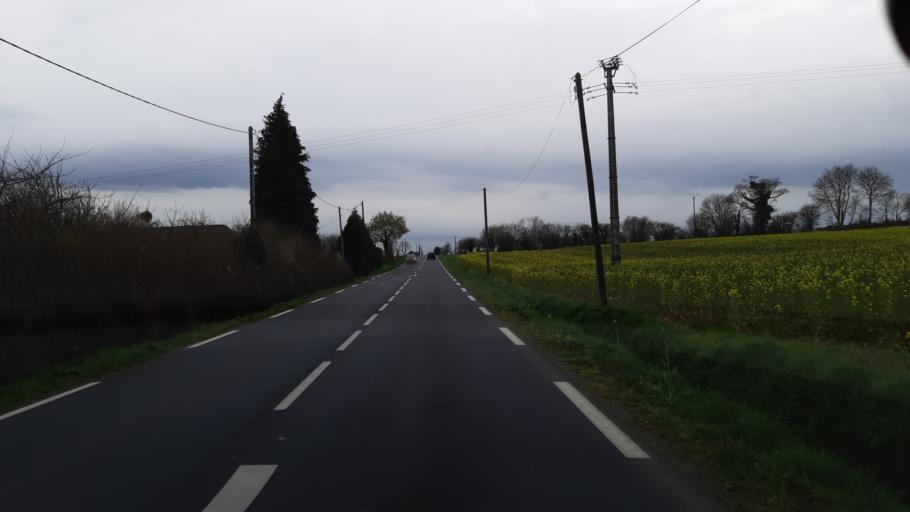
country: FR
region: Lower Normandy
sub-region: Departement de la Manche
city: Percy
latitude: 48.9885
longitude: -1.1575
